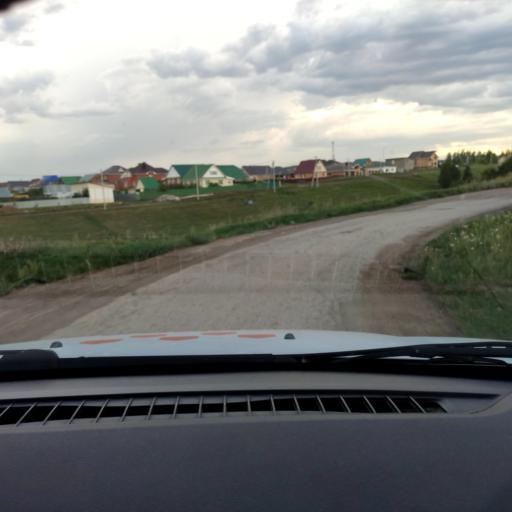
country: RU
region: Bashkortostan
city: Chishmy
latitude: 54.6083
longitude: 55.3964
